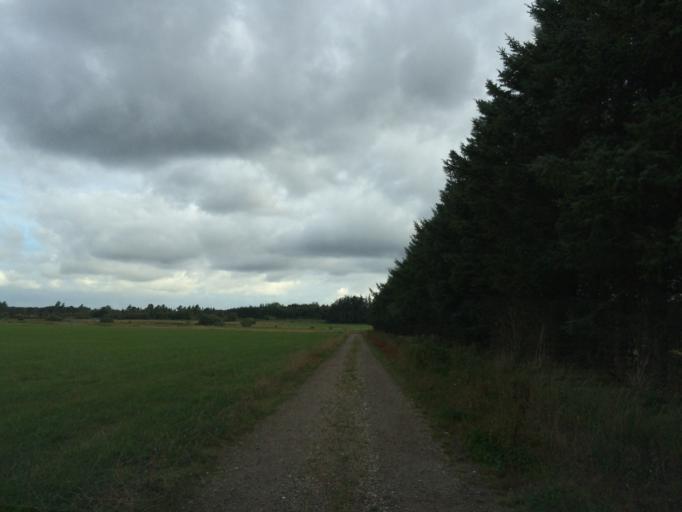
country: DK
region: Central Jutland
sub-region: Holstebro Kommune
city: Ulfborg
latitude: 56.2437
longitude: 8.4180
